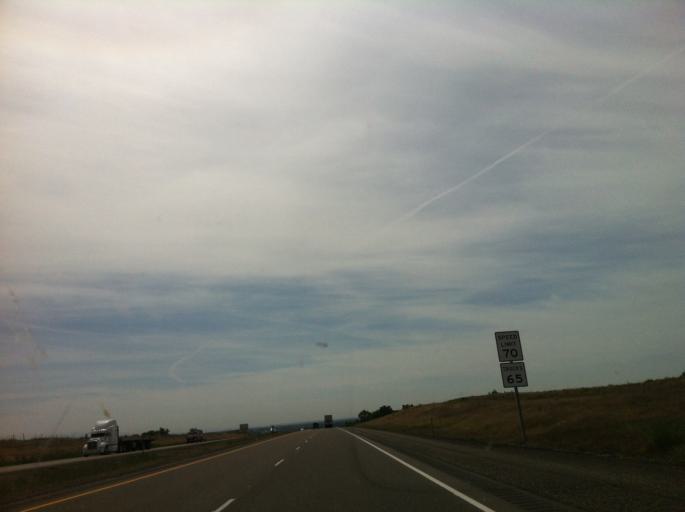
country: US
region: Oregon
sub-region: Malheur County
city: Ontario
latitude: 44.0796
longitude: -117.0117
